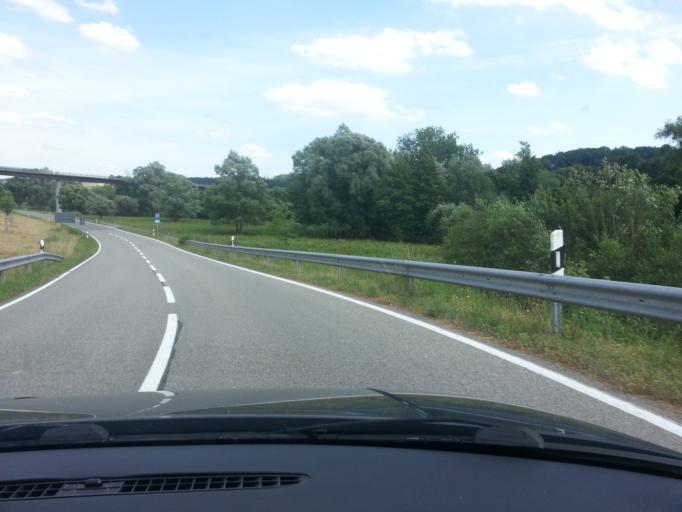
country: DE
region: Rheinland-Pfalz
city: Hornbach
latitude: 49.1864
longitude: 7.3771
